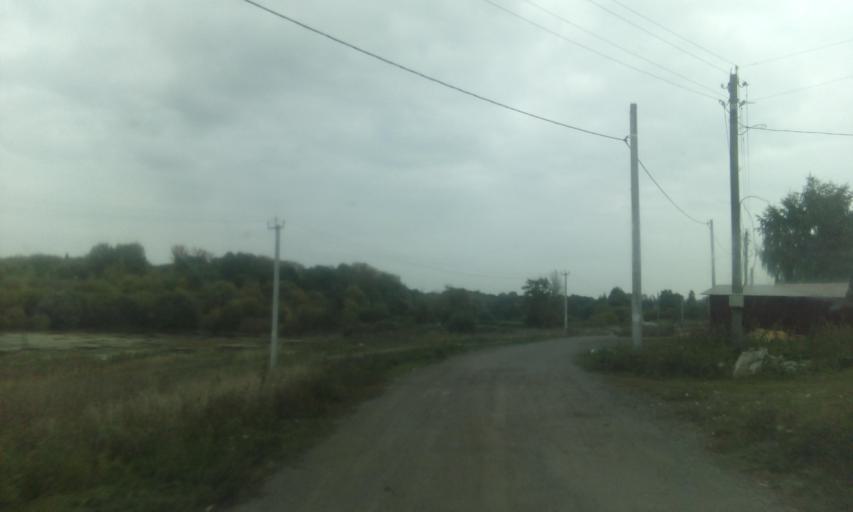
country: RU
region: Tula
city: Dubovka
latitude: 53.9476
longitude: 38.0256
